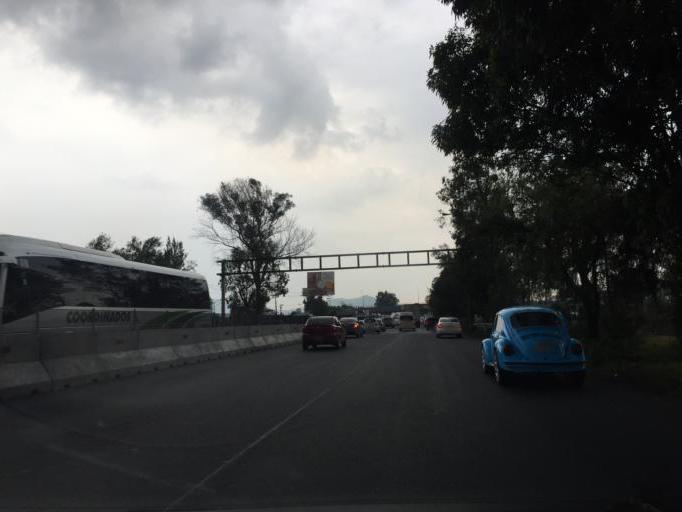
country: MX
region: Mexico
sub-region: Tultitlan
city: Buenavista
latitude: 19.6259
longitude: -99.1928
